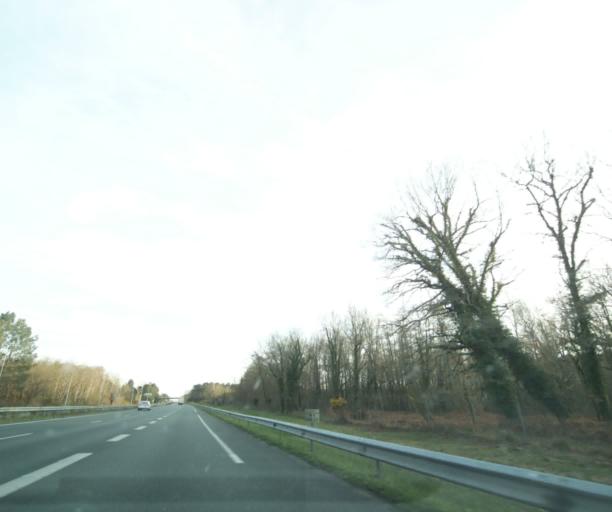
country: FR
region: Aquitaine
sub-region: Departement de la Gironde
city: Reignac
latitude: 45.1863
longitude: -0.4909
